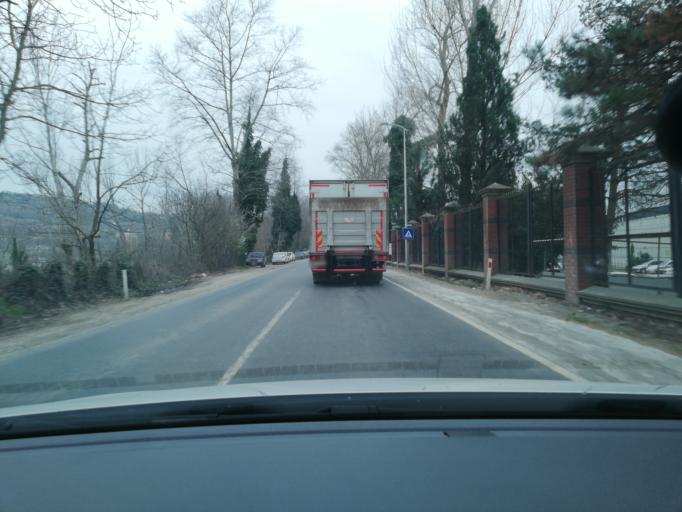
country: TR
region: Zonguldak
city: Gokcebey
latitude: 41.3026
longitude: 32.1238
